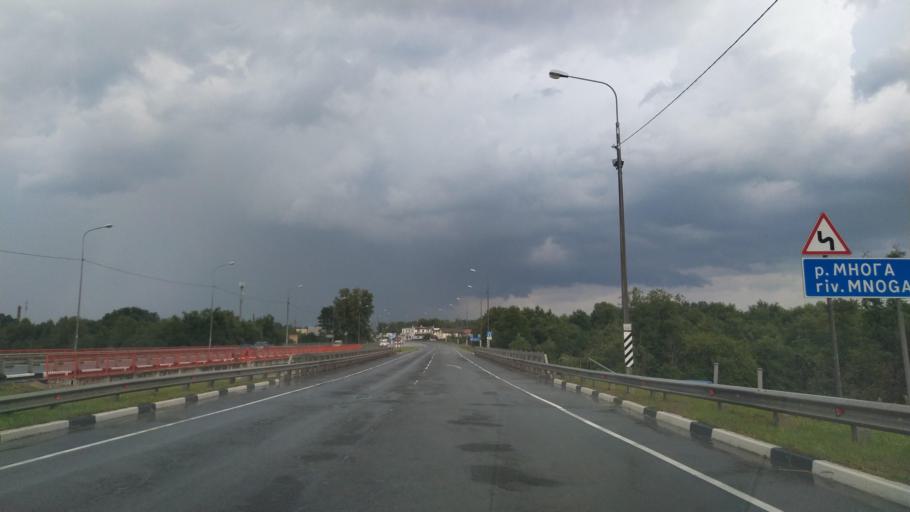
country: RU
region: Pskov
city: Pskov
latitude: 57.7412
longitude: 28.3673
